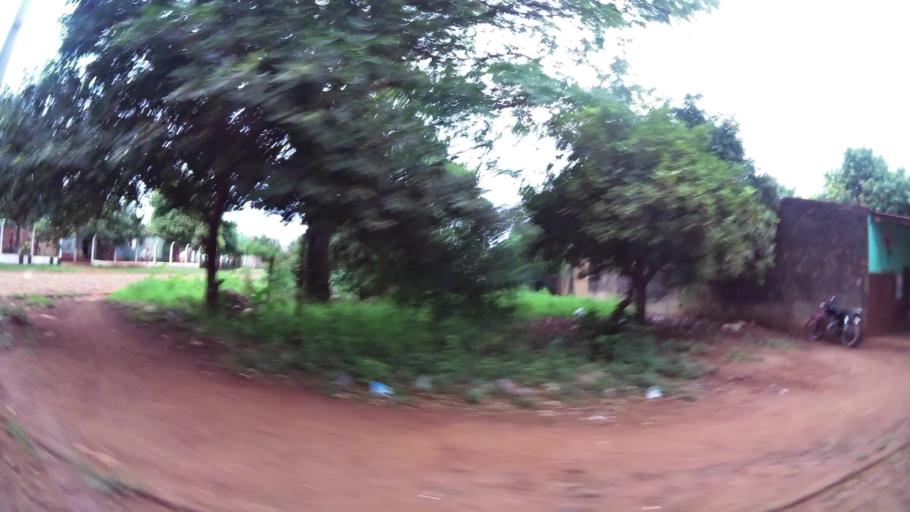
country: PY
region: Alto Parana
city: Presidente Franco
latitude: -25.5484
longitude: -54.6544
